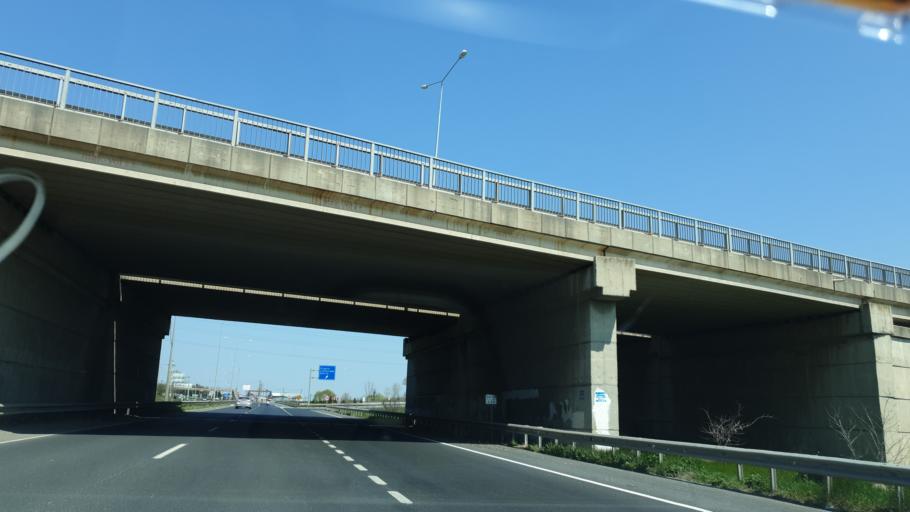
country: TR
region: Tekirdag
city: Corlu
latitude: 41.1784
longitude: 27.8094
